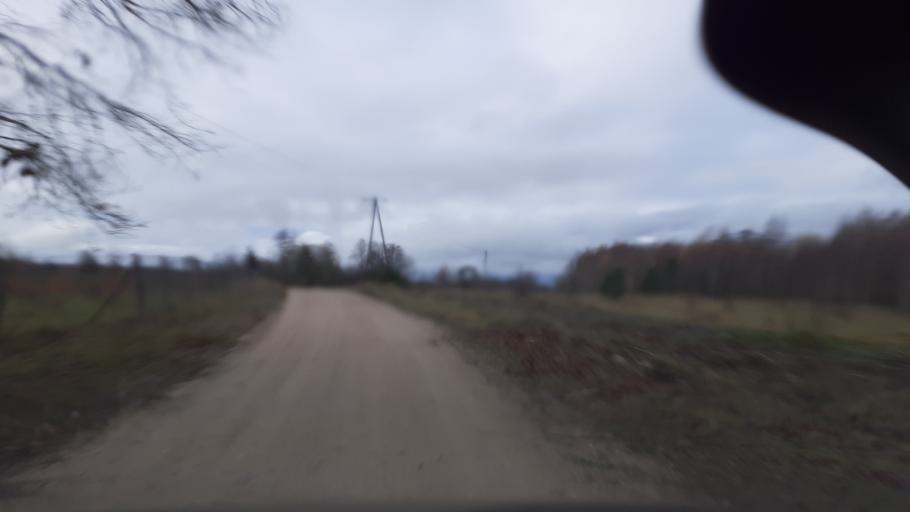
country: LV
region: Kuldigas Rajons
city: Kuldiga
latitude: 57.0419
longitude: 21.8763
